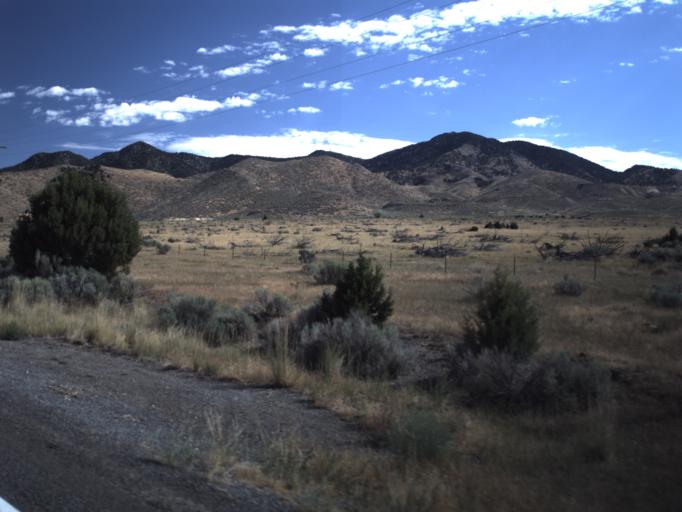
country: US
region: Utah
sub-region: Juab County
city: Mona
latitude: 39.9012
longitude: -112.1380
